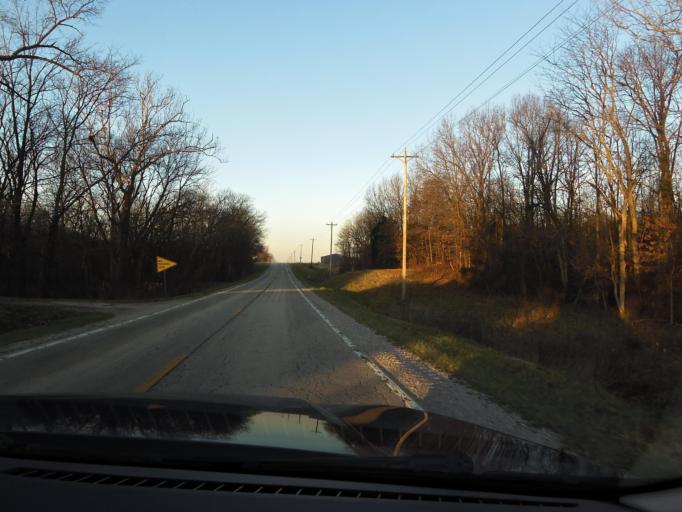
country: US
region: Illinois
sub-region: Marion County
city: Salem
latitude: 38.7653
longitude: -88.9821
